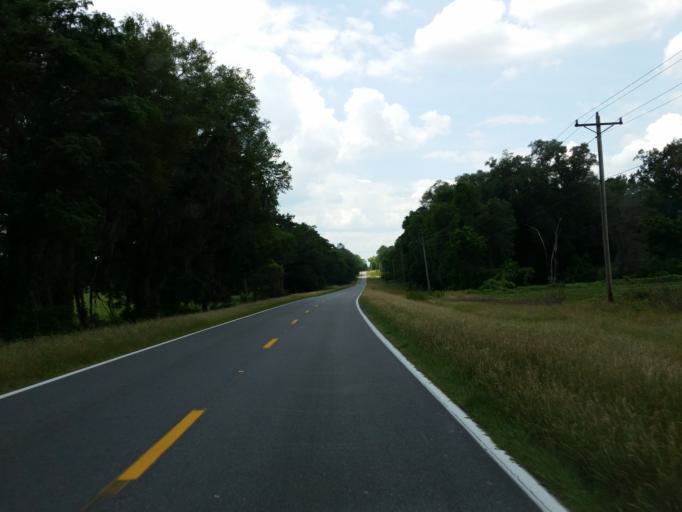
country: US
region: Florida
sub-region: Alachua County
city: High Springs
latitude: 29.9525
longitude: -82.5956
